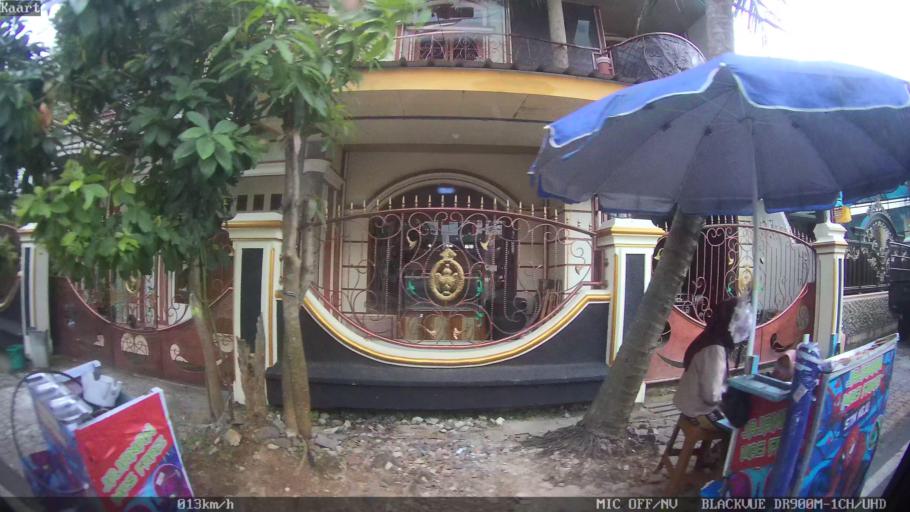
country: ID
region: Lampung
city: Bandarlampung
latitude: -5.4262
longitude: 105.2560
